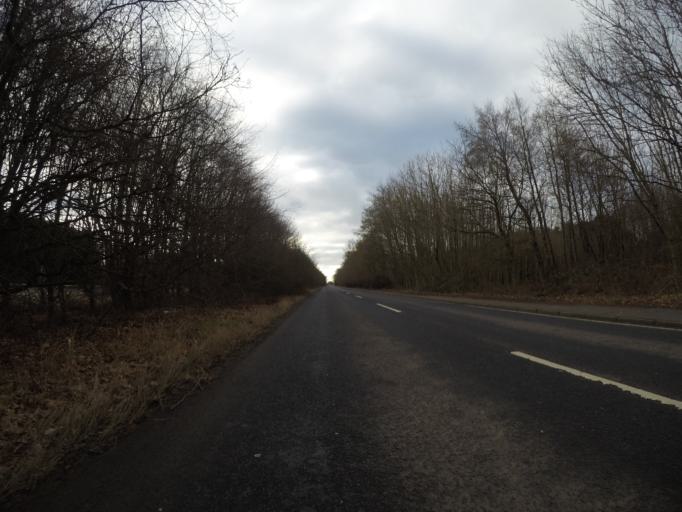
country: GB
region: Scotland
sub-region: North Ayrshire
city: Dreghorn
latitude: 55.5807
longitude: -4.6442
